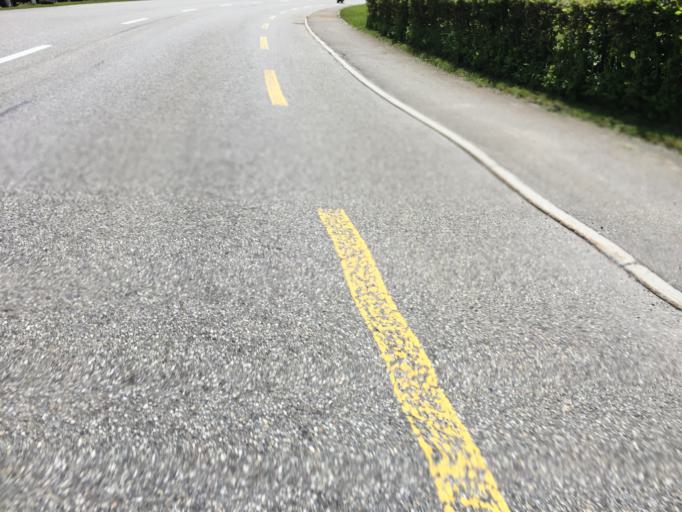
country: CH
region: Bern
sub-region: Emmental District
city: Trub
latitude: 46.9109
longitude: 7.8795
